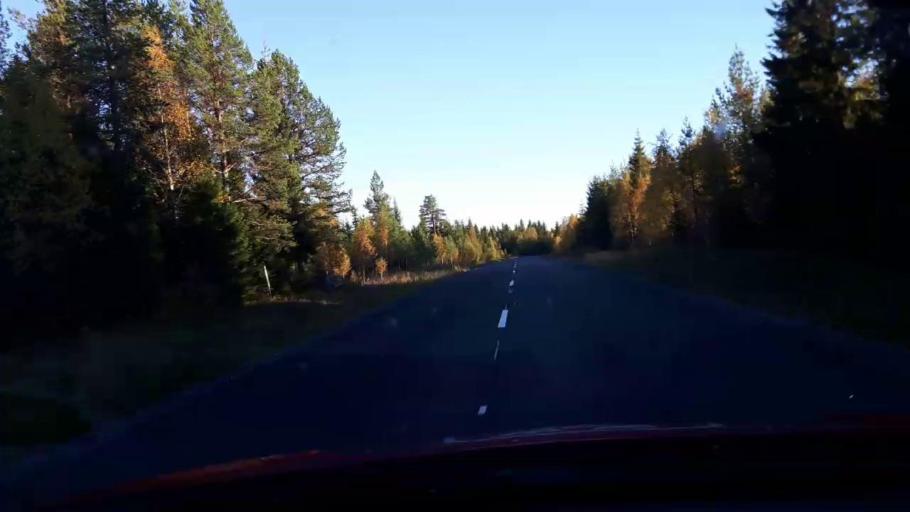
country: SE
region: Jaemtland
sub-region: OEstersunds Kommun
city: Lit
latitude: 63.4900
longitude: 14.8783
